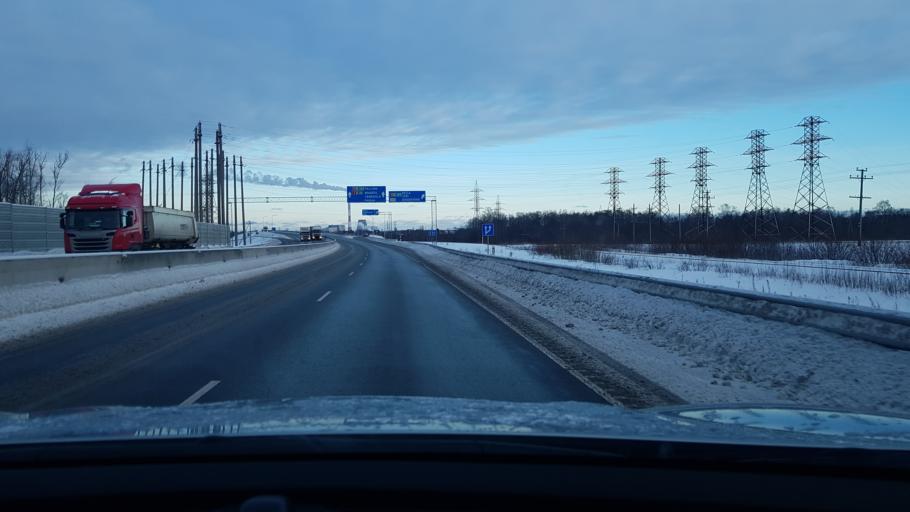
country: EE
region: Harju
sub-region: Joelaehtme vald
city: Loo
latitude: 59.4206
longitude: 24.9209
